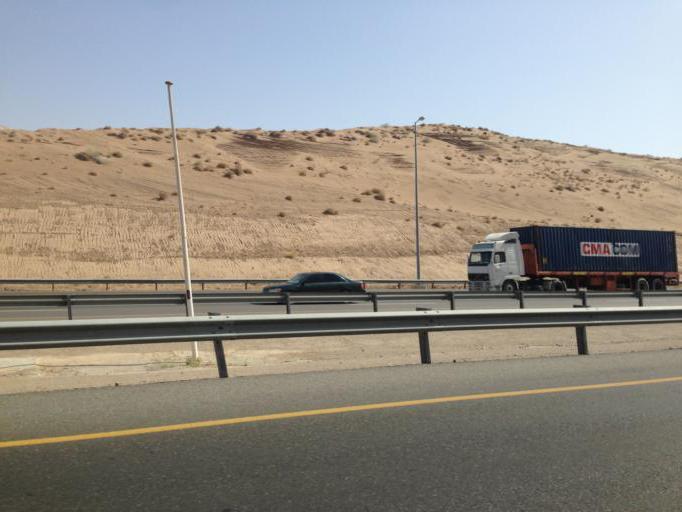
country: OM
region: Muhafazat Masqat
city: Bawshar
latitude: 23.5711
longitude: 58.4205
